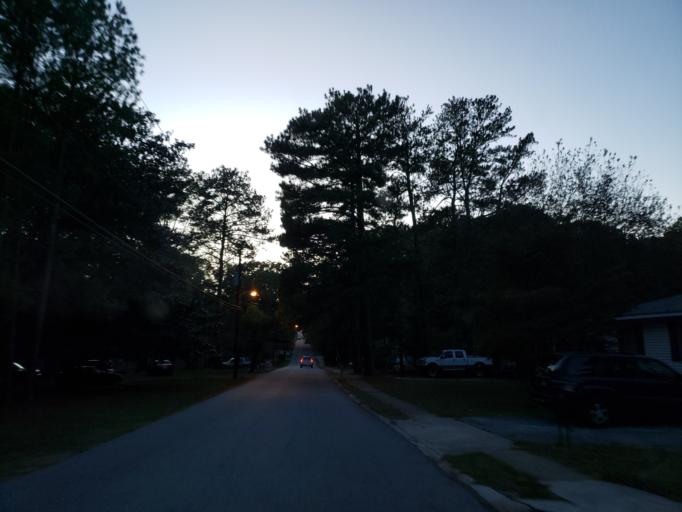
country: US
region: Georgia
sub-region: Cobb County
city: Fair Oaks
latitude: 33.9129
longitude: -84.5487
